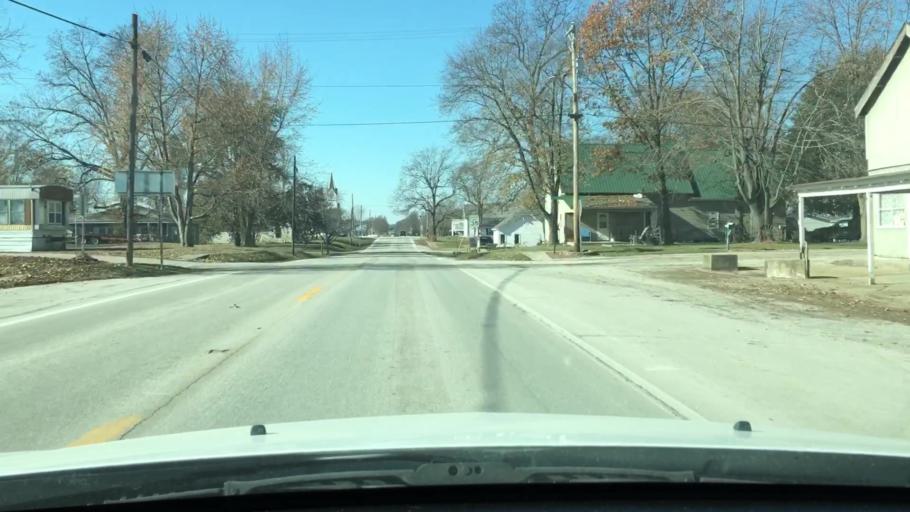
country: US
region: Illinois
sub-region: Pike County
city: Griggsville
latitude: 39.6203
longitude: -90.6766
